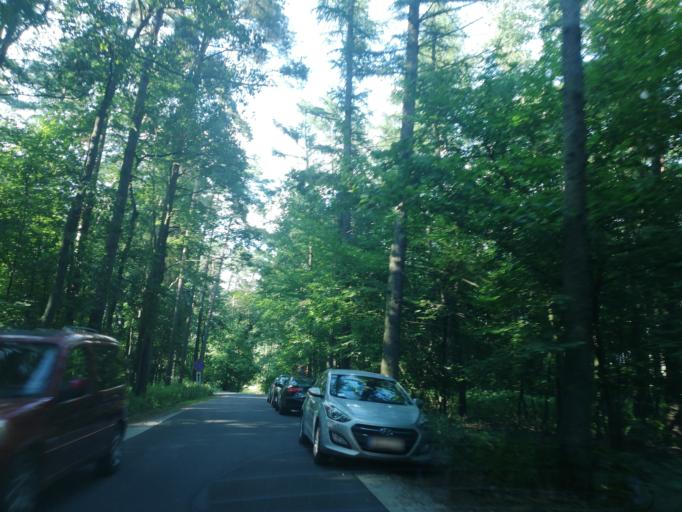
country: PL
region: Kujawsko-Pomorskie
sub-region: Powiat golubsko-dobrzynski
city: Ciechocin
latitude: 53.0787
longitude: 18.9500
